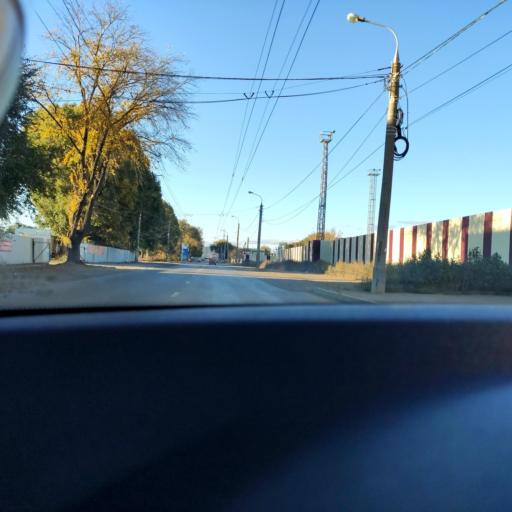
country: RU
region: Samara
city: Samara
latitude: 53.1987
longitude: 50.2683
